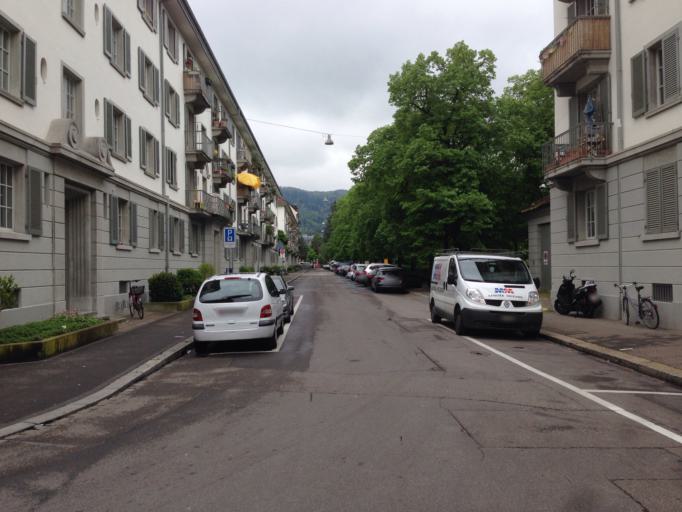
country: CH
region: Zurich
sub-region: Bezirk Zuerich
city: Zuerich (Kreis 3) / Sihlfeld
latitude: 47.3766
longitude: 8.5137
